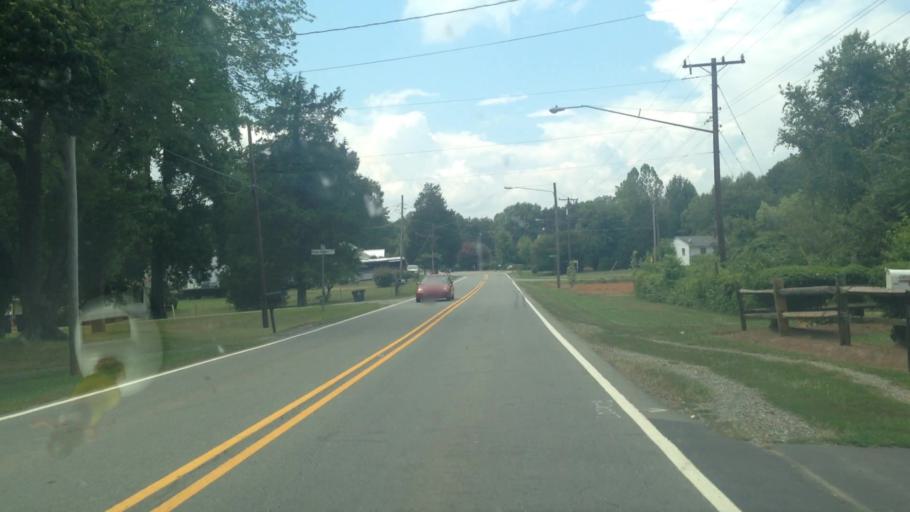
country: US
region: North Carolina
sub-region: Forsyth County
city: Rural Hall
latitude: 36.1927
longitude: -80.2478
